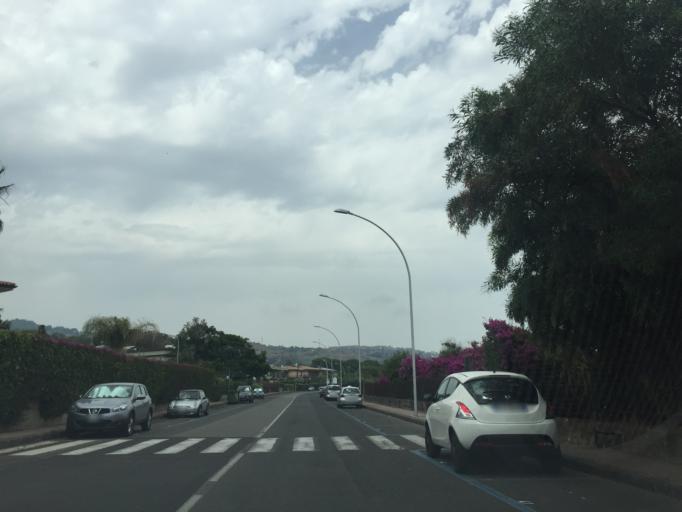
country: IT
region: Sicily
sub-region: Catania
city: Aci Castello
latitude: 37.5463
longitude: 15.1438
